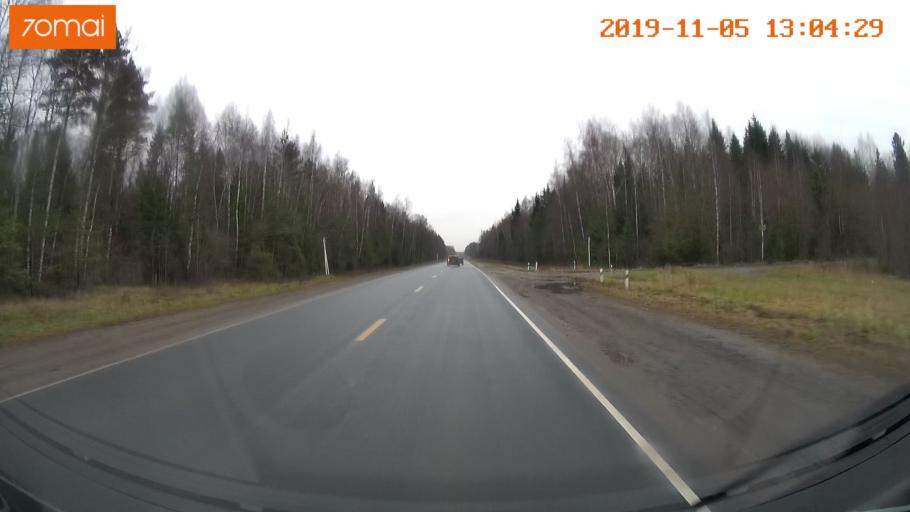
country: RU
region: Ivanovo
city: Kitovo
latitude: 56.8887
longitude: 41.2223
